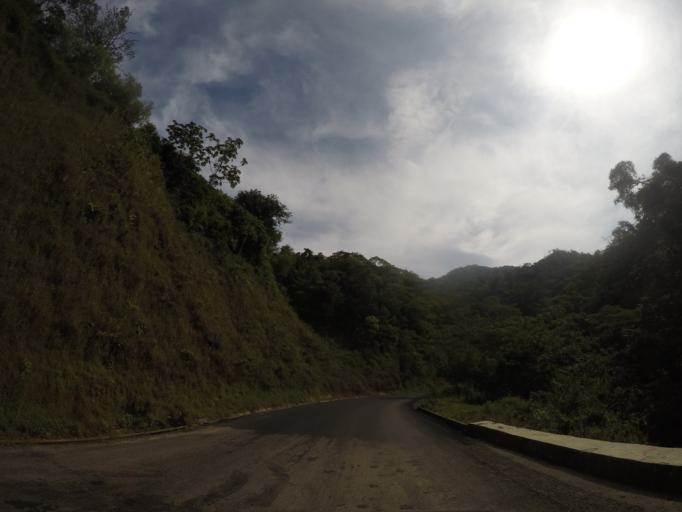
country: MX
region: Oaxaca
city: Pluma Hidalgo
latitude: 15.9333
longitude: -96.4267
